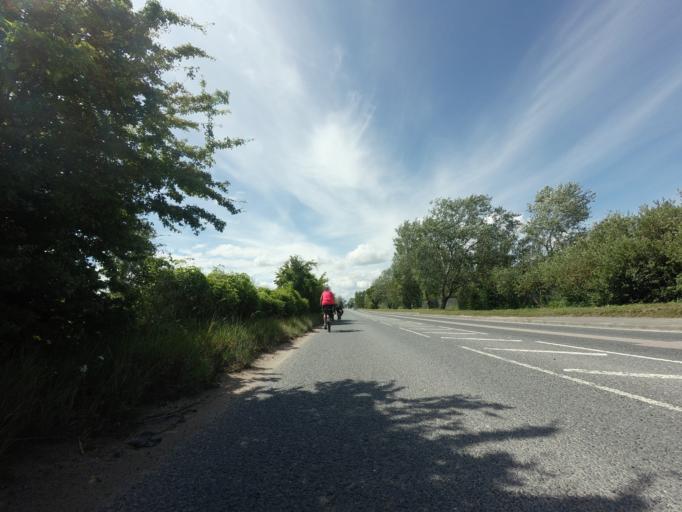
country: GB
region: England
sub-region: Medway
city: Allhallows
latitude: 51.4443
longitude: 0.6839
